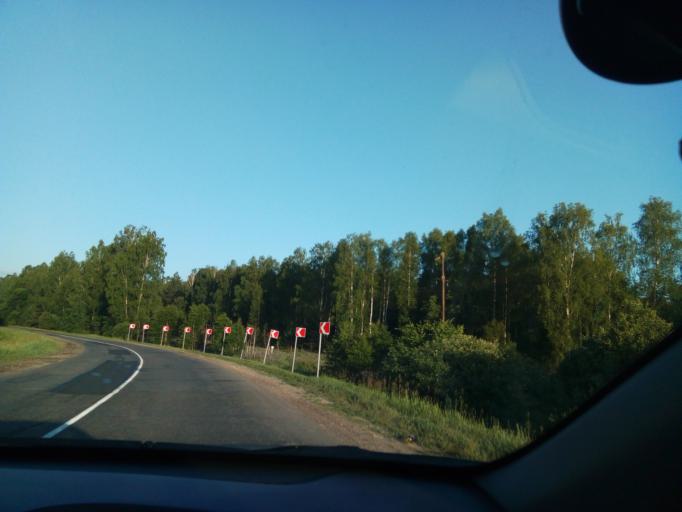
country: RU
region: Nizjnij Novgorod
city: Satis
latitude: 54.9293
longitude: 43.1957
